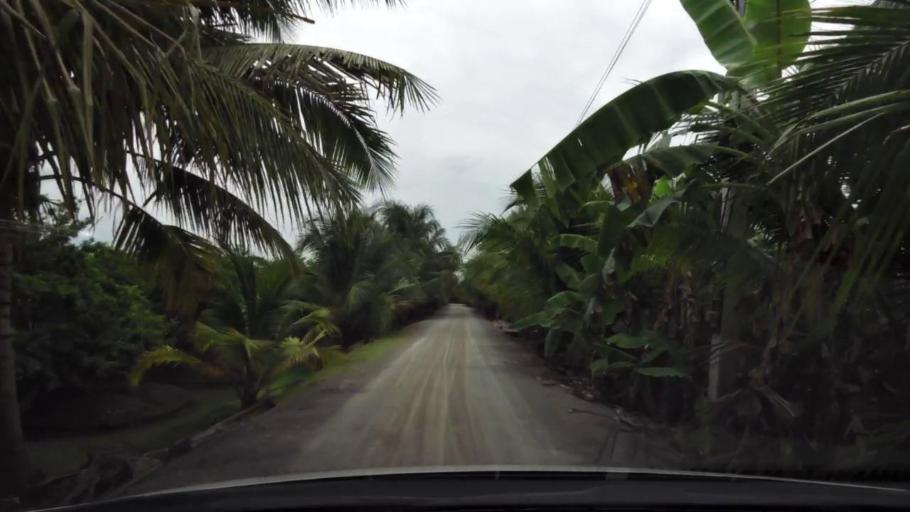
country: TH
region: Ratchaburi
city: Damnoen Saduak
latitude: 13.5633
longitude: 100.0162
